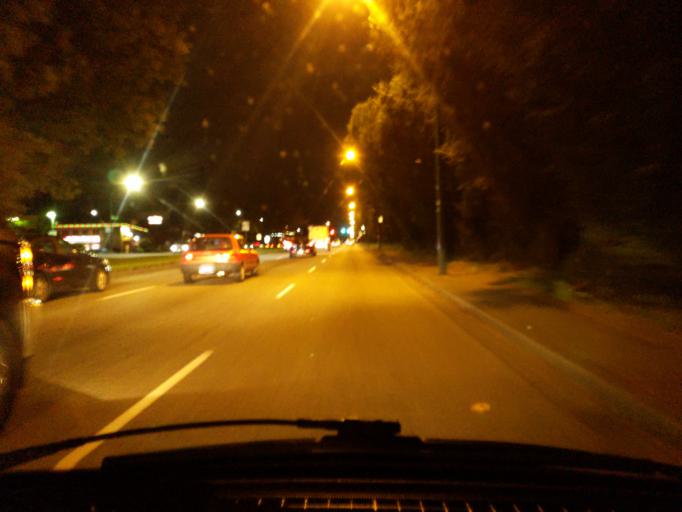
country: CA
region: British Columbia
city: Burnaby
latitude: 49.2572
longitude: -123.0238
